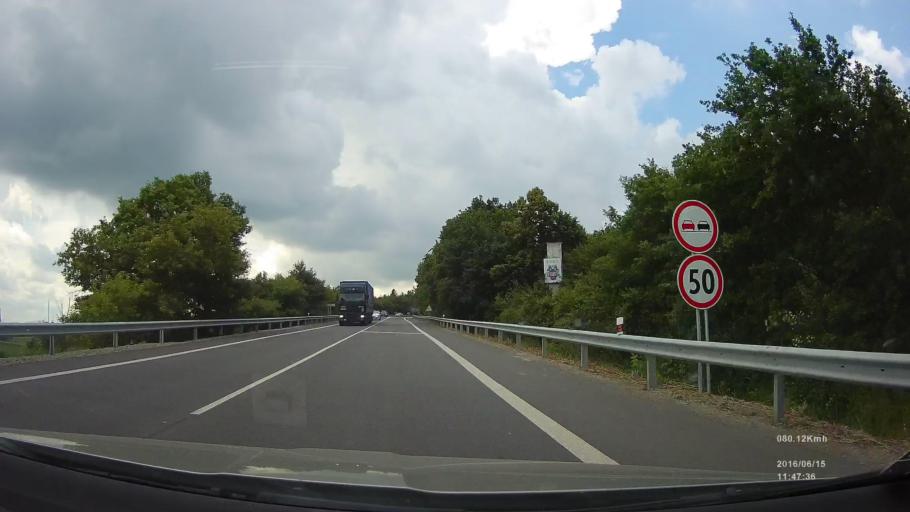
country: SK
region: Kosicky
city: Kosice
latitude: 48.7302
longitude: 21.3274
